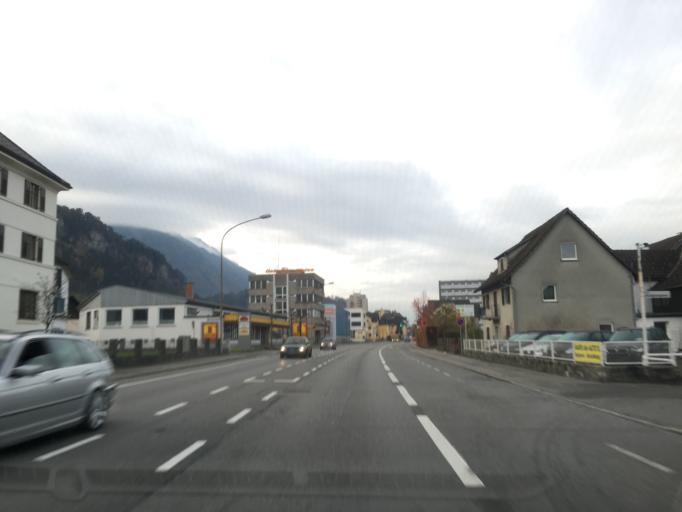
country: AT
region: Vorarlberg
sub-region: Politischer Bezirk Feldkirch
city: Feldkirch
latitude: 47.2460
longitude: 9.6086
